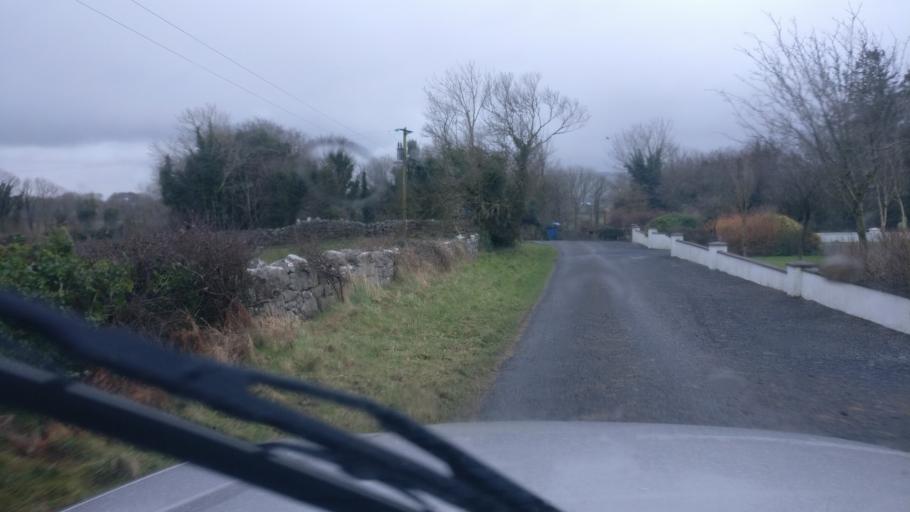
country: IE
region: Connaught
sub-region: County Galway
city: Loughrea
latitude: 53.1910
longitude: -8.6793
